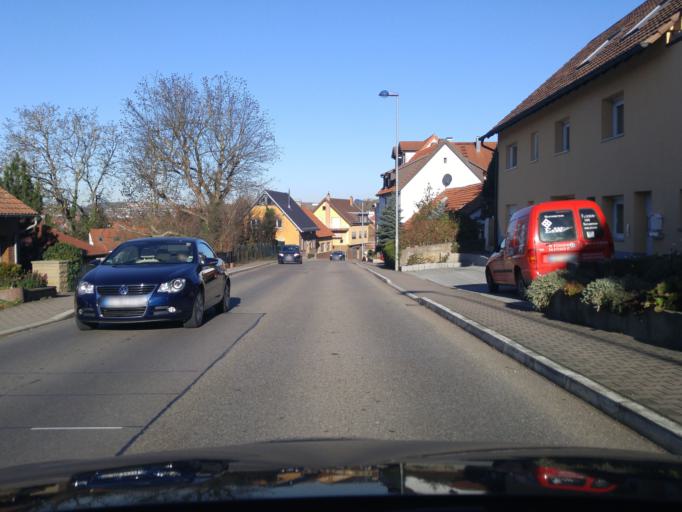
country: DE
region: Baden-Wuerttemberg
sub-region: Karlsruhe Region
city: Sinsheim
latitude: 49.2365
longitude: 8.9114
